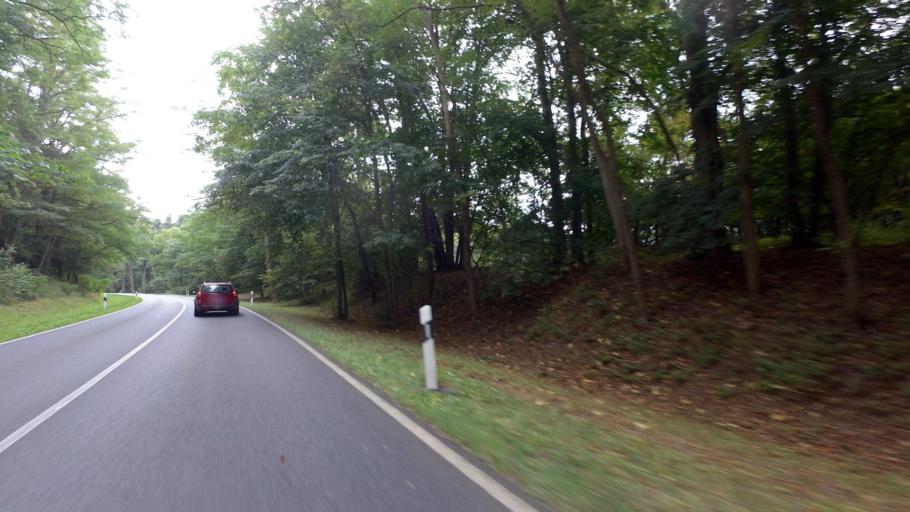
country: DE
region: Brandenburg
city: Luckau
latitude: 51.7699
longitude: 13.6850
